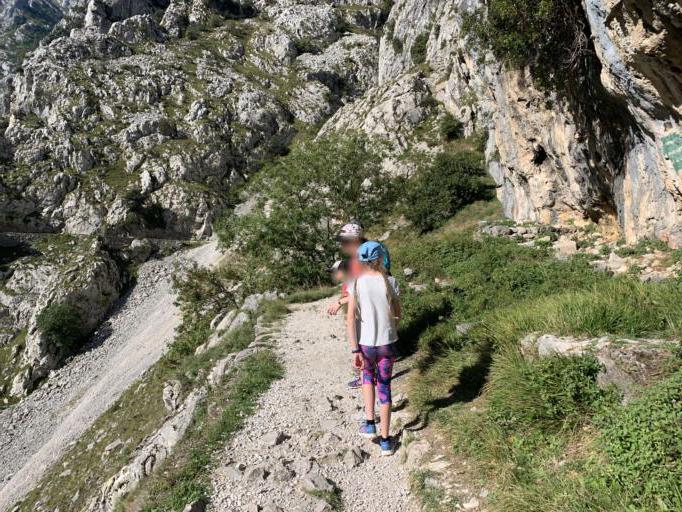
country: ES
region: Asturias
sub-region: Province of Asturias
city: Carrena
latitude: 43.2495
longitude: -4.8815
